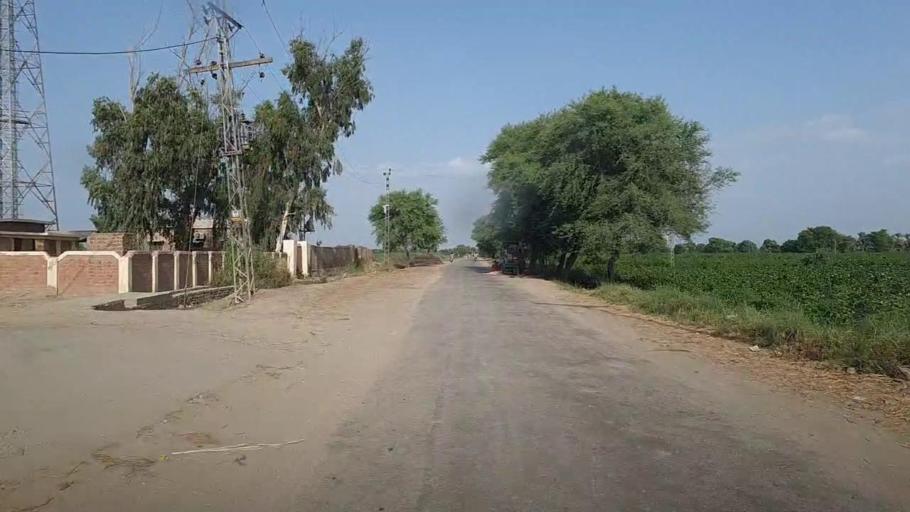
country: PK
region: Sindh
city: Khairpur
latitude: 28.0767
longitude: 69.7982
